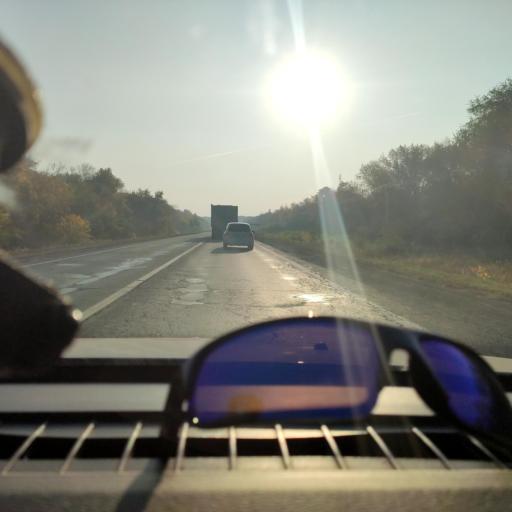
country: RU
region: Samara
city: Novokuybyshevsk
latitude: 52.9857
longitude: 49.8680
